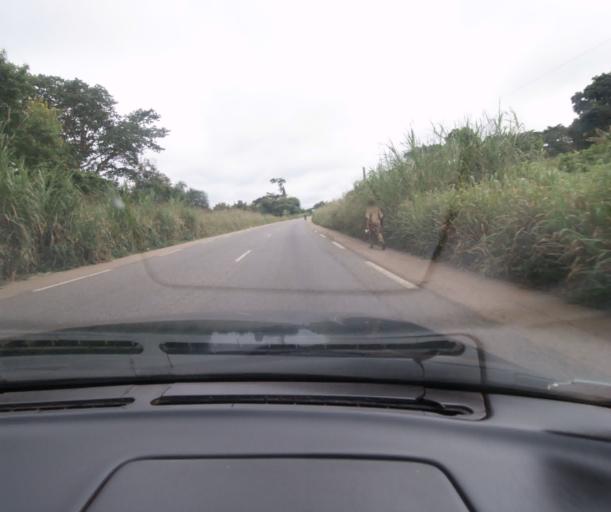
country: CM
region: Centre
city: Ombesa
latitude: 4.5987
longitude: 11.2580
